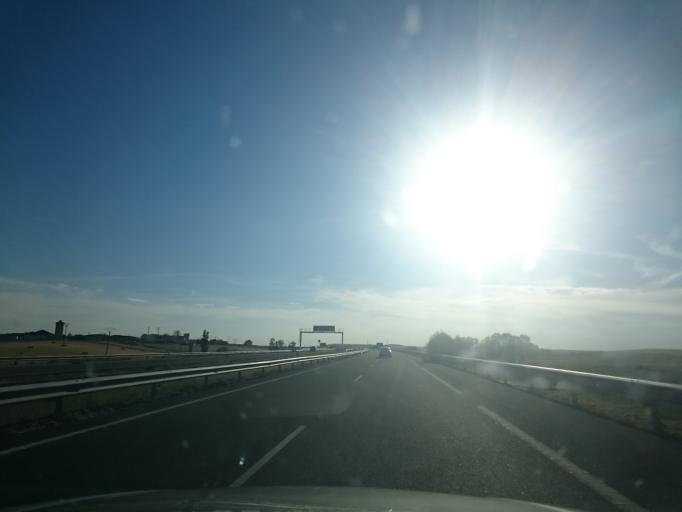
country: ES
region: Castille and Leon
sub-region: Provincia de Palencia
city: Villaherreros
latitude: 42.3927
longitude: -4.4558
